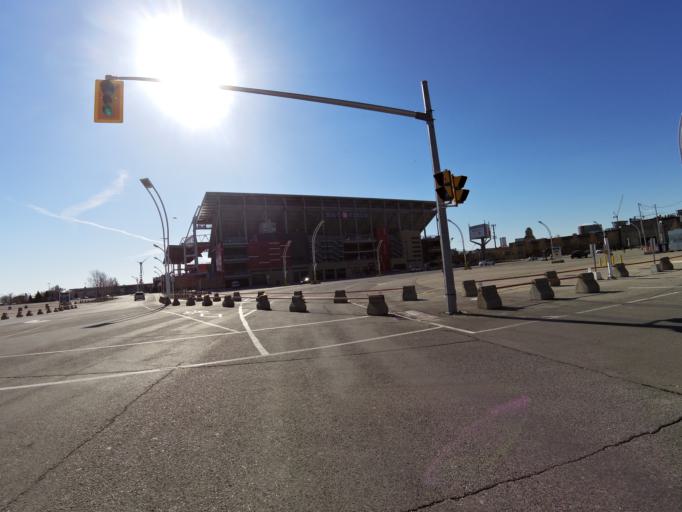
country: CA
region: Ontario
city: Toronto
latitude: 43.6332
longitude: -79.4153
